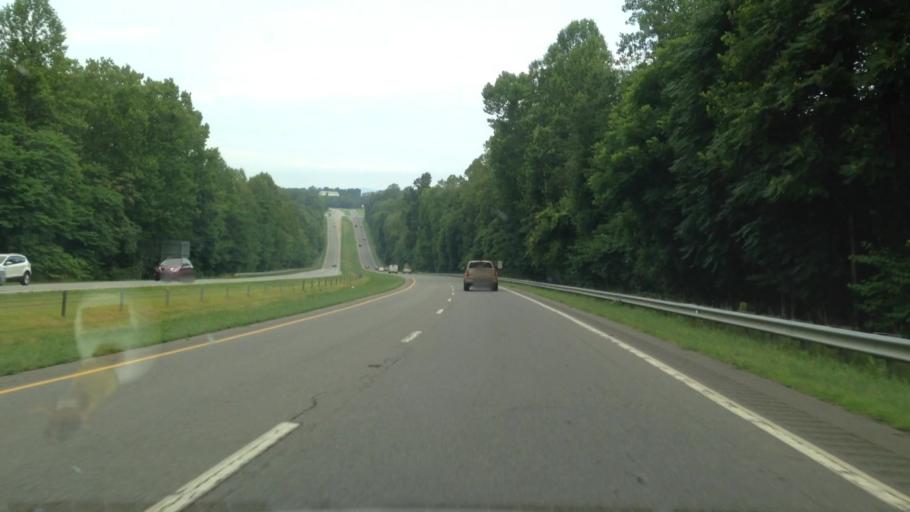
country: US
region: North Carolina
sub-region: Surry County
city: Flat Rock
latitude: 36.4636
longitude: -80.5639
